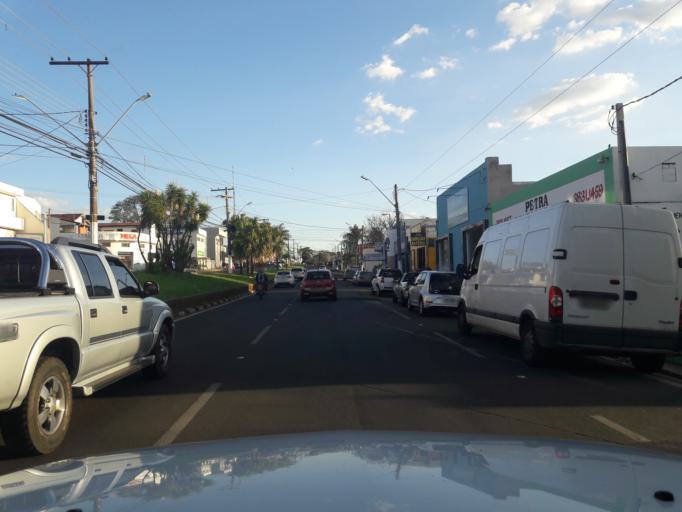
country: BR
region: Sao Paulo
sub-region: Moji-Guacu
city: Mogi-Gaucu
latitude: -22.3947
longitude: -46.9467
